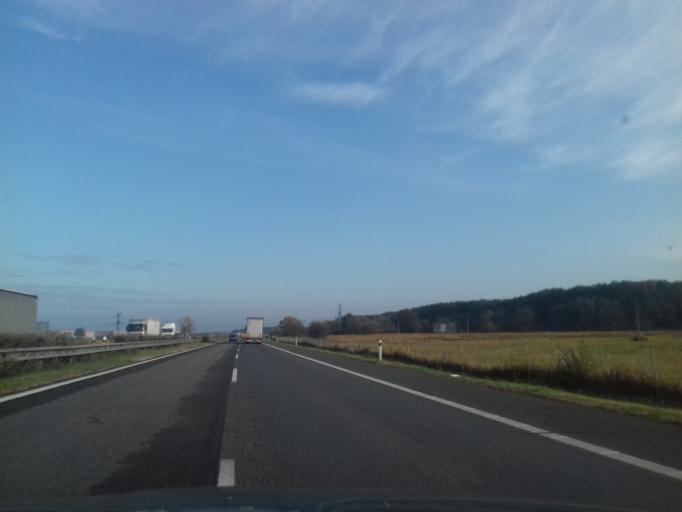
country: SK
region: Bratislavsky
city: Stupava
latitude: 48.3052
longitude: 17.0160
